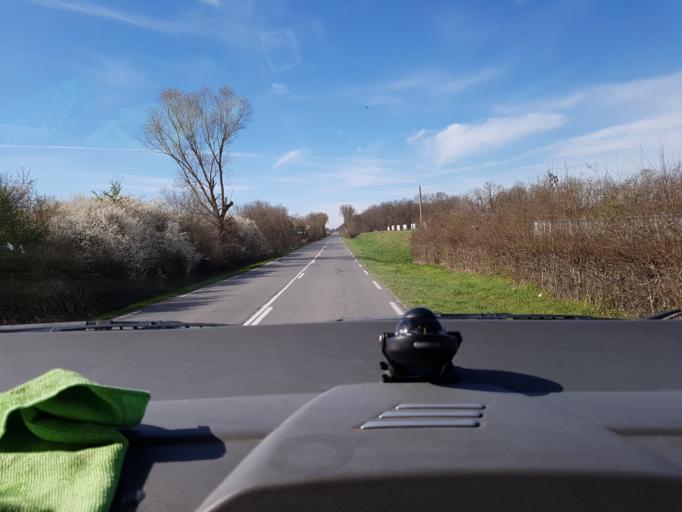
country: FR
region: Bourgogne
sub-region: Departement de Saone-et-Loire
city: Gueugnon
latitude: 46.5699
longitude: 4.0571
